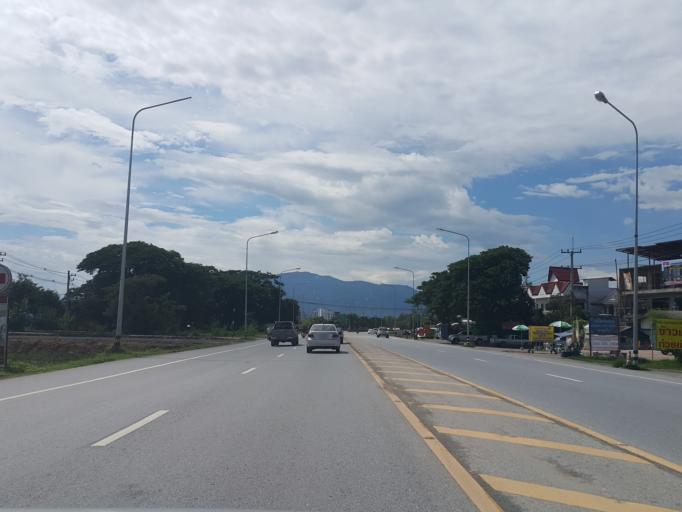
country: TH
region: Chiang Mai
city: Saraphi
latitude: 18.7604
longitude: 99.0435
